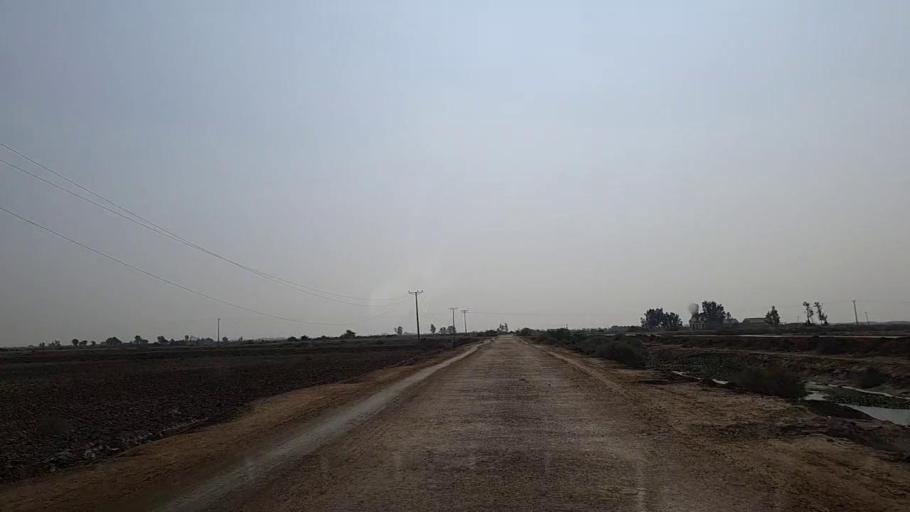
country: PK
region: Sindh
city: Thatta
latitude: 24.7133
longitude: 67.7684
